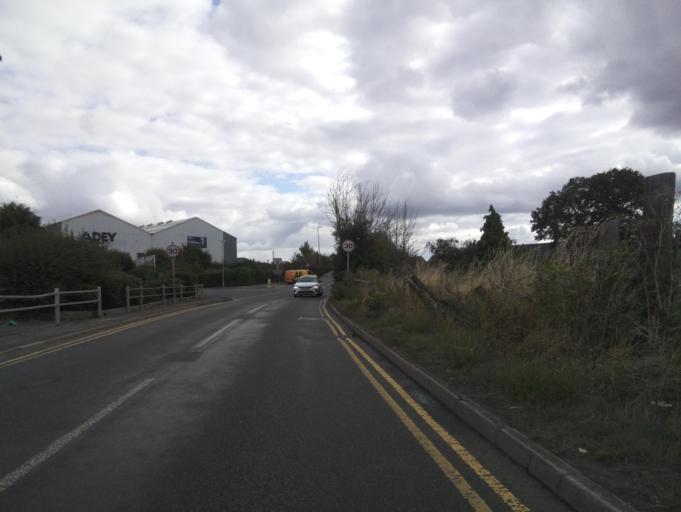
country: GB
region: England
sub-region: Leicestershire
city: Loughborough
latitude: 52.7841
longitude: -1.2013
